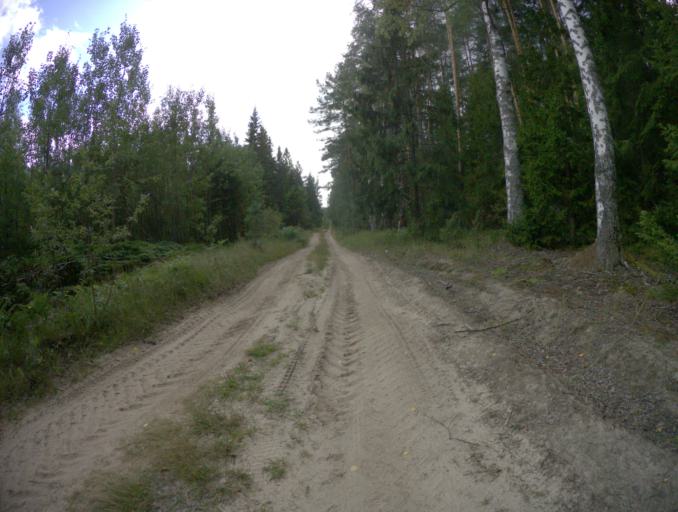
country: RU
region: Vladimir
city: Vorsha
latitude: 55.9556
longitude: 40.1490
